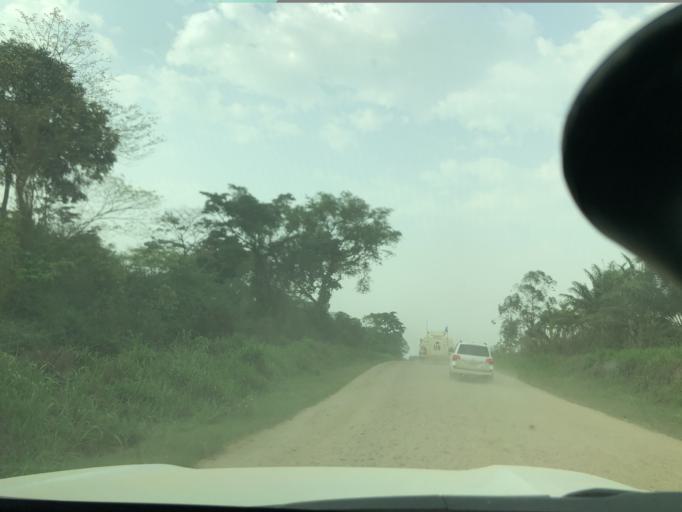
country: UG
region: Western Region
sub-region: Kasese District
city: Margherita
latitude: 0.2441
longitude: 29.6787
